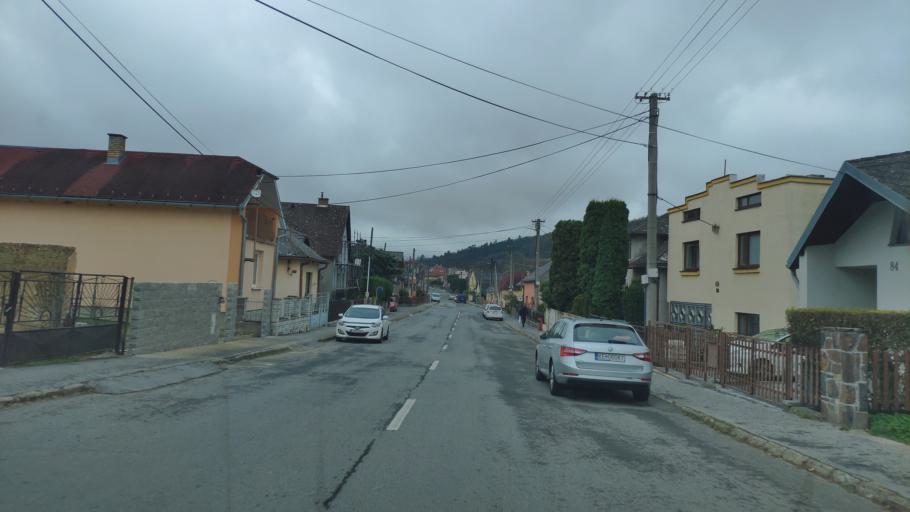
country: SK
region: Presovsky
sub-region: Okres Presov
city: Presov
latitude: 49.0698
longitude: 21.2057
